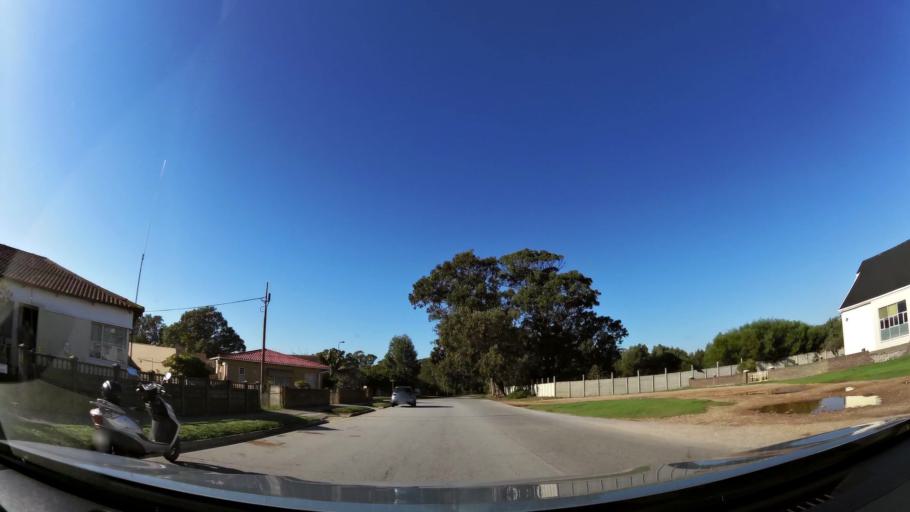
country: ZA
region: Eastern Cape
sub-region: Nelson Mandela Bay Metropolitan Municipality
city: Port Elizabeth
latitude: -33.9842
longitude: 25.6323
